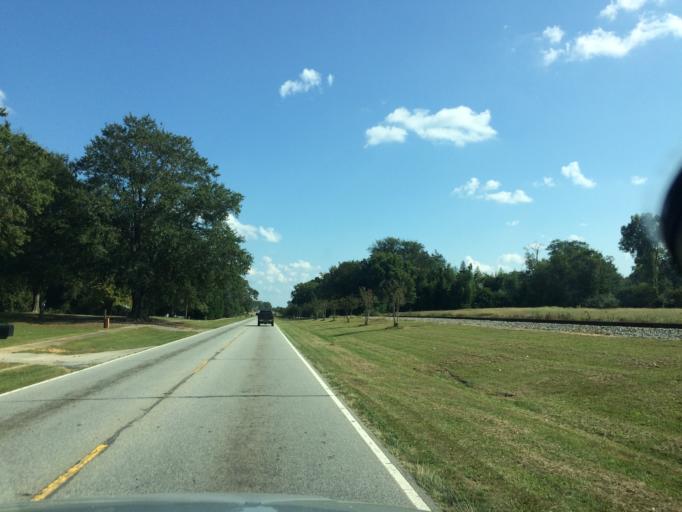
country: US
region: South Carolina
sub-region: Greenville County
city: Fountain Inn
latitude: 34.6150
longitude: -82.1199
